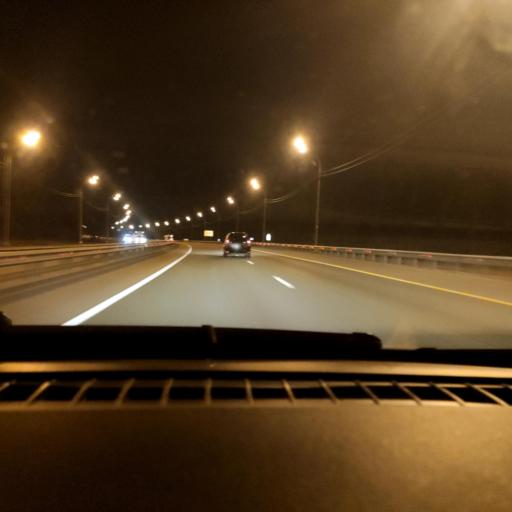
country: RU
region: Lipetsk
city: Khlevnoye
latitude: 52.2469
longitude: 39.0656
